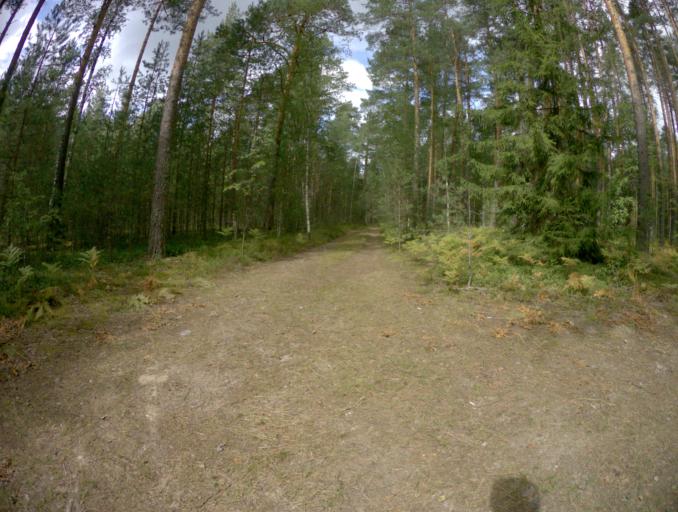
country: RU
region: Vladimir
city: Raduzhnyy
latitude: 55.9653
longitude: 40.2146
